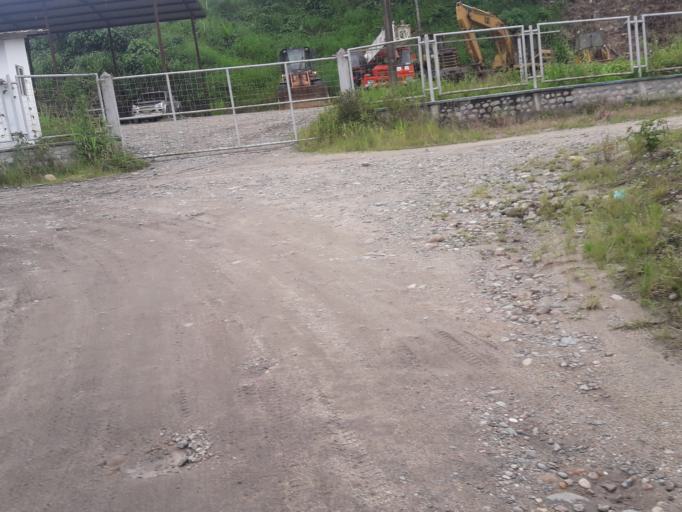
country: EC
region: Napo
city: Tena
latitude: -0.9882
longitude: -77.8110
